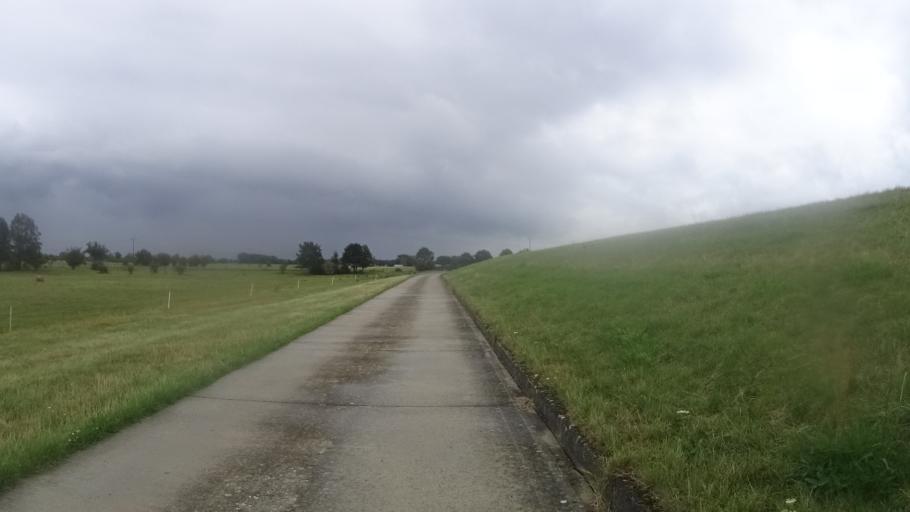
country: DE
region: Lower Saxony
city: Neu Darchau
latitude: 53.2555
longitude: 10.8617
